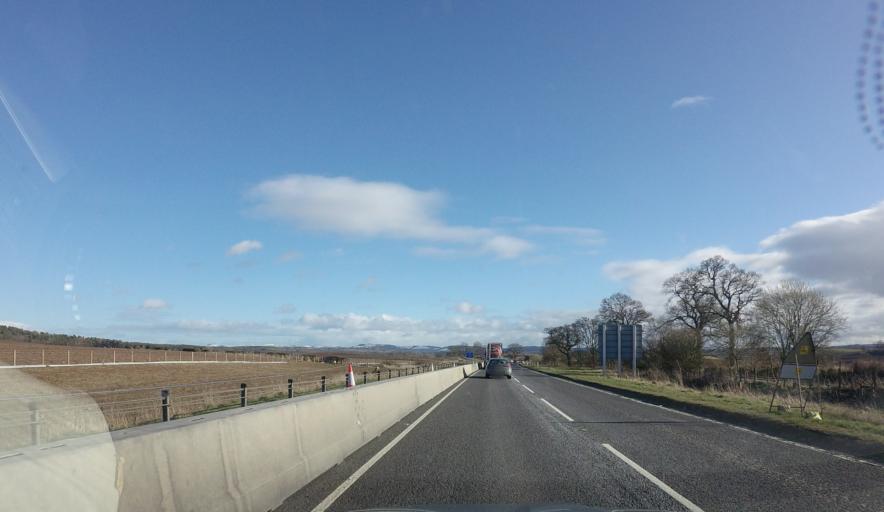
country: GB
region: Scotland
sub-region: Perth and Kinross
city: Bankfoot
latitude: 56.4795
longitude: -3.4928
